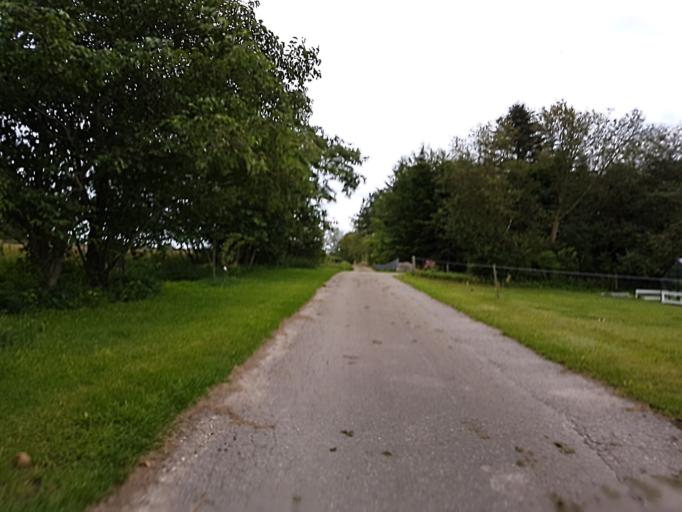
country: DK
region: Capital Region
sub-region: Egedal Kommune
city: Stenlose
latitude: 55.7915
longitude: 12.1939
